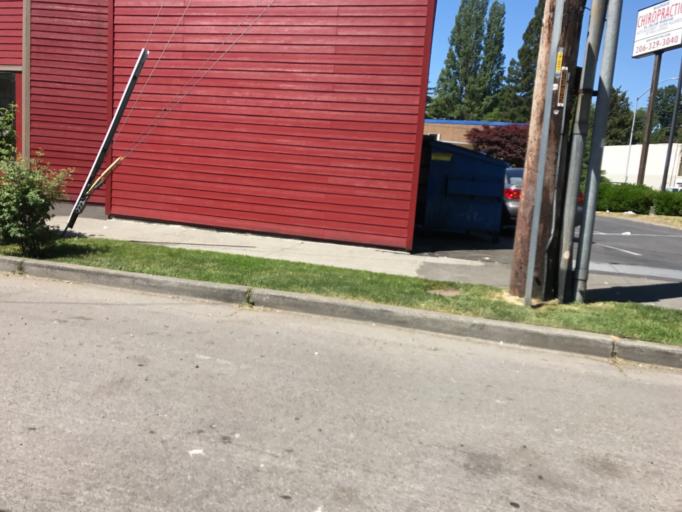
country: US
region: Washington
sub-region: King County
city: Seattle
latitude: 47.5820
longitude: -122.3003
